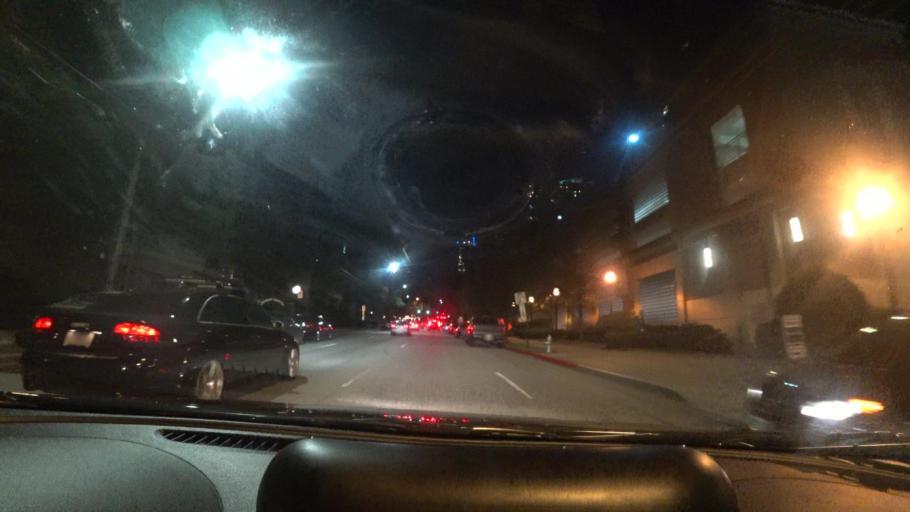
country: US
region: Georgia
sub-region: Fulton County
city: Atlanta
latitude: 33.7807
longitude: -84.3826
